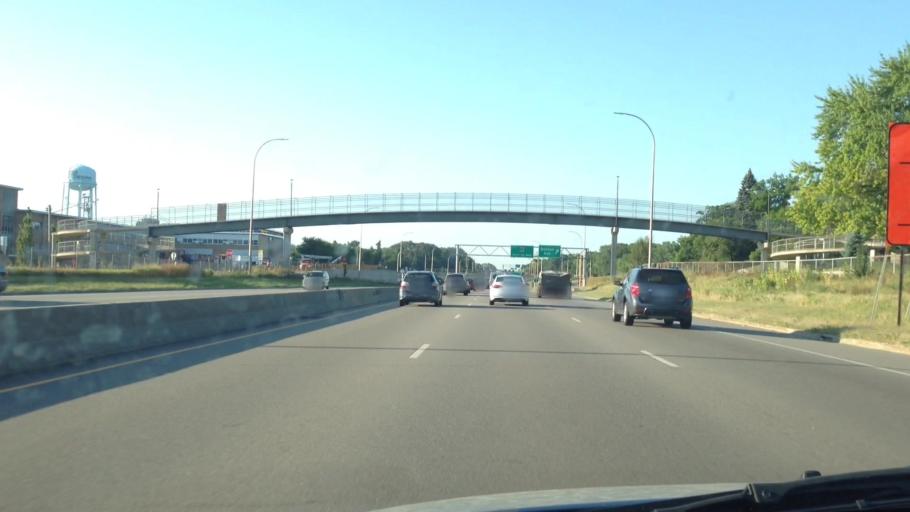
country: US
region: Minnesota
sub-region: Hennepin County
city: Edina
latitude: 44.9010
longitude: -93.3505
